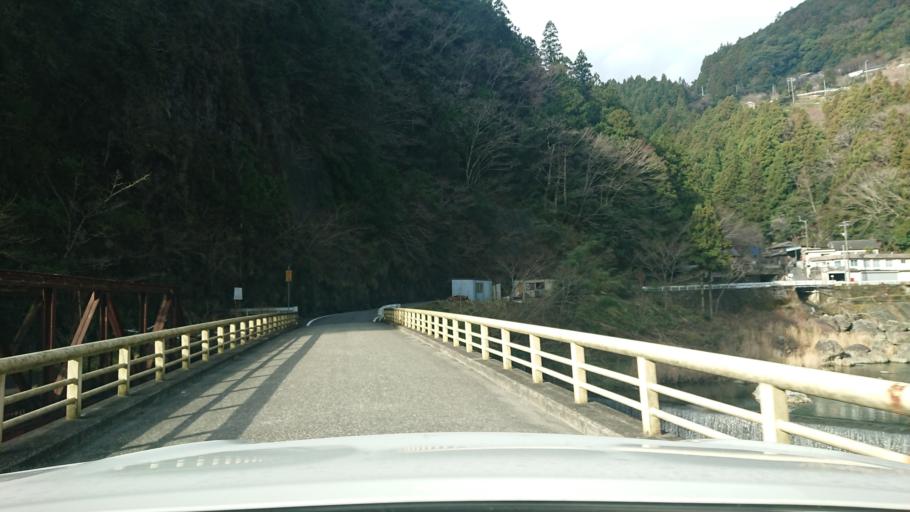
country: JP
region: Tokushima
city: Ishii
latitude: 33.8960
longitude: 134.3988
